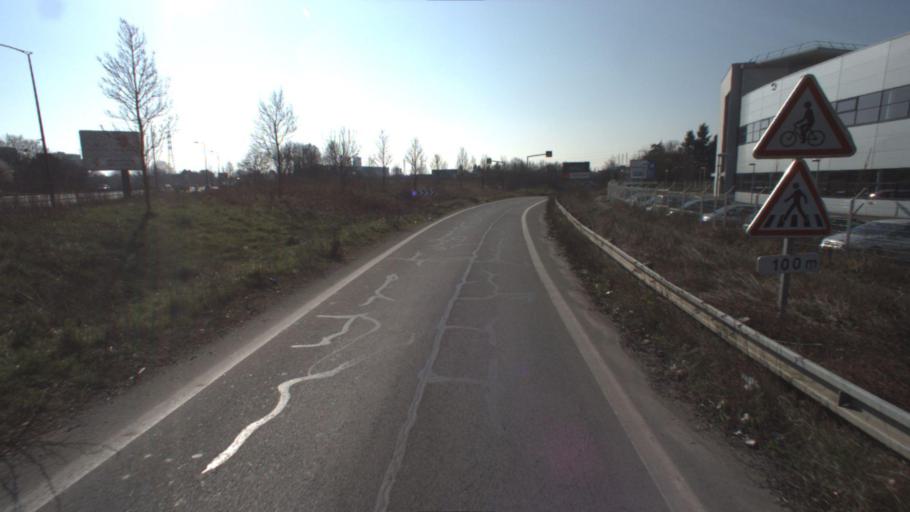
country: FR
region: Ile-de-France
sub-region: Departement de l'Essonne
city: Evry
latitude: 48.6179
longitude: 2.4536
